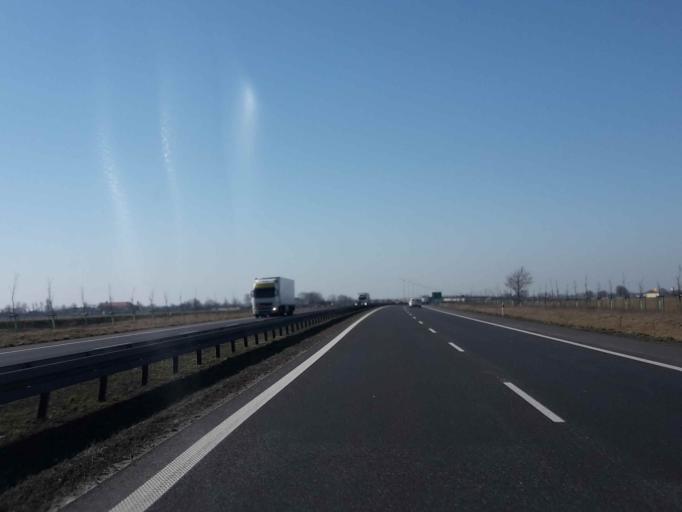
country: PL
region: Greater Poland Voivodeship
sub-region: Powiat poznanski
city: Kleszczewo
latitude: 52.3464
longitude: 17.1737
